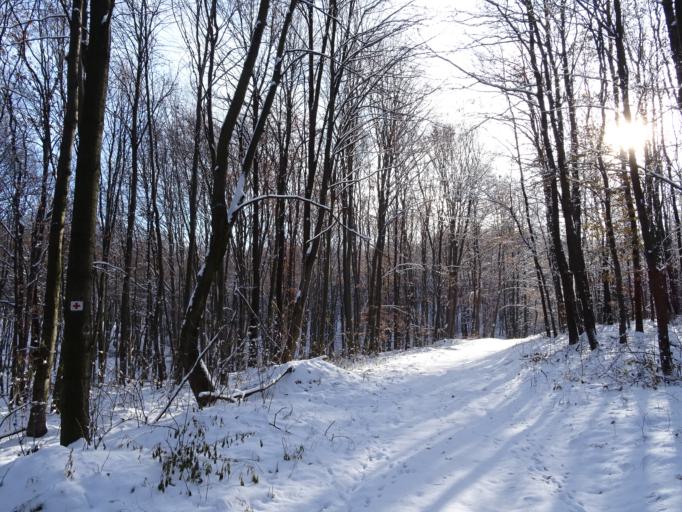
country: HU
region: Fejer
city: Mor
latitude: 47.3821
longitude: 18.2550
